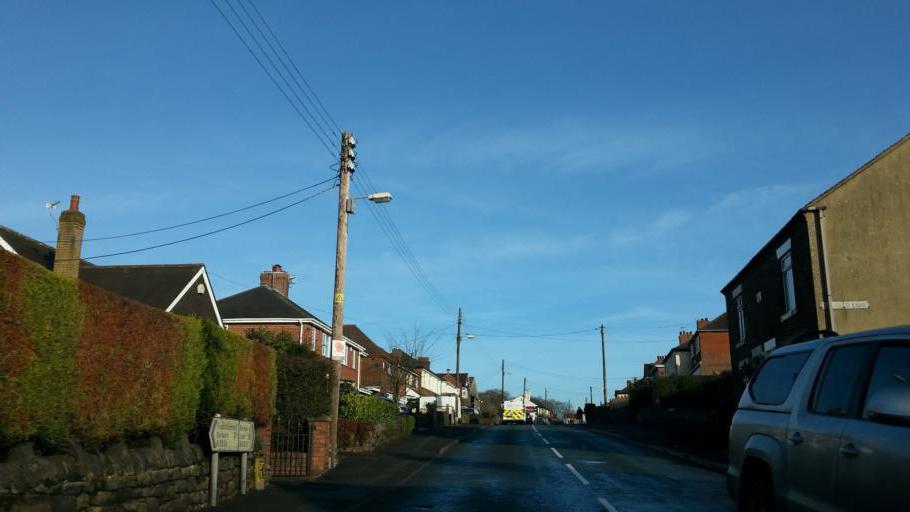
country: GB
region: England
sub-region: Staffordshire
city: Biddulph
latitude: 53.0753
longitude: -2.1392
